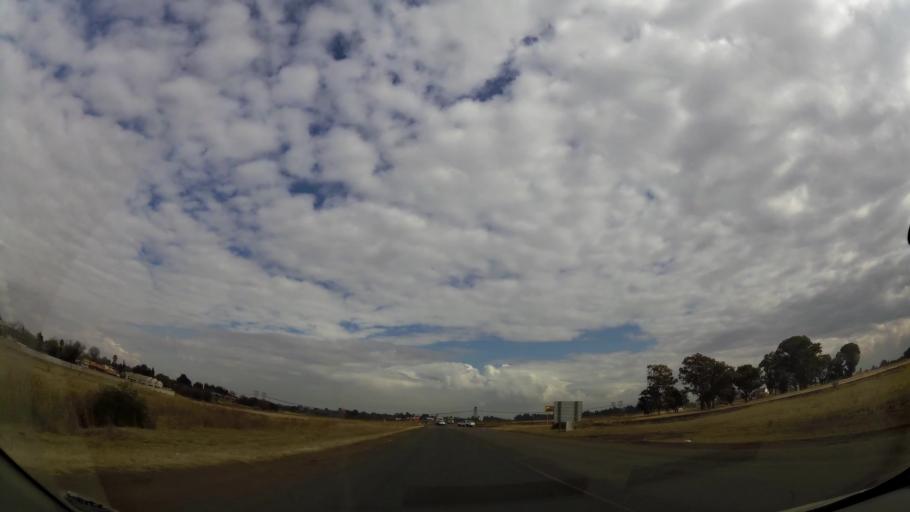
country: ZA
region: Gauteng
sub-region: Sedibeng District Municipality
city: Vereeniging
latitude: -26.6505
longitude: 28.0126
